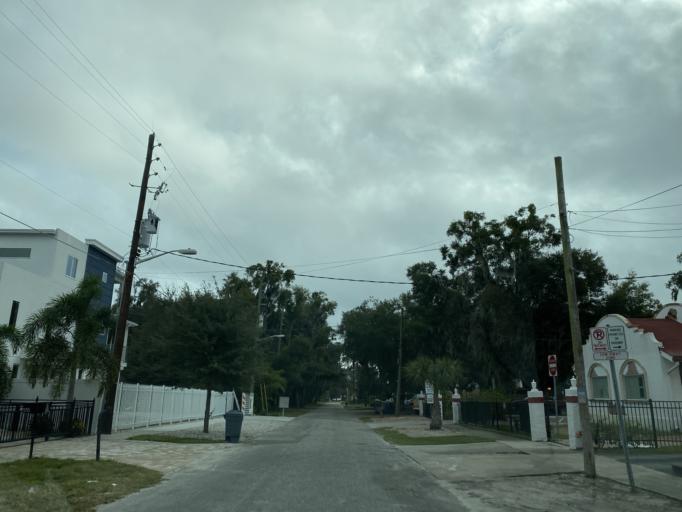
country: US
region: Florida
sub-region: Orange County
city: Orlando
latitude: 28.5536
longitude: -81.3875
